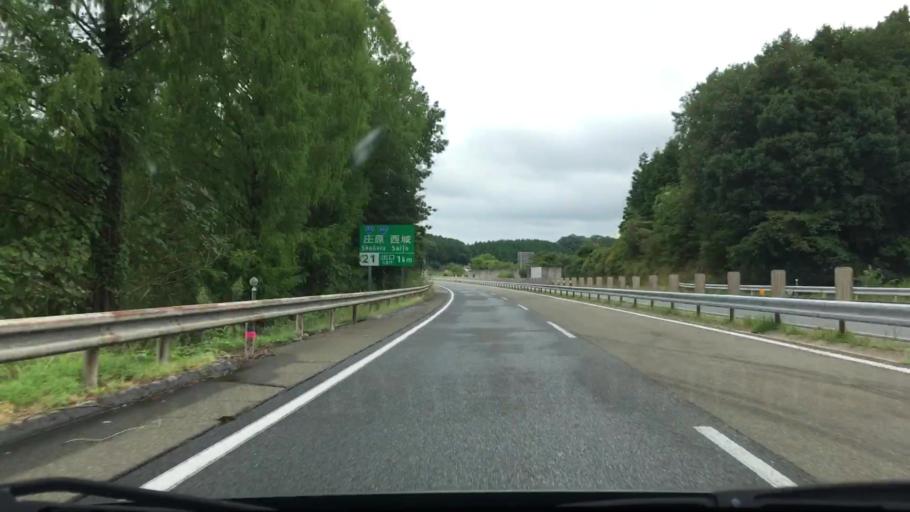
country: JP
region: Hiroshima
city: Shobara
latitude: 34.8426
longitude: 133.0383
